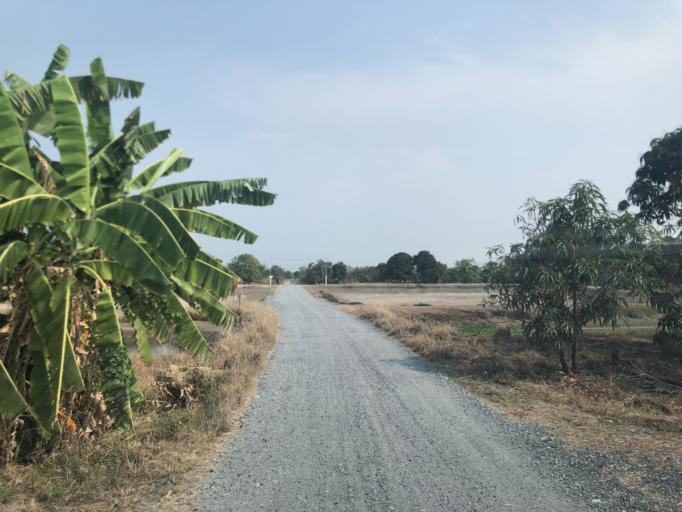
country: TH
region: Chachoengsao
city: Bang Pakong
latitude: 13.5169
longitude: 100.9179
